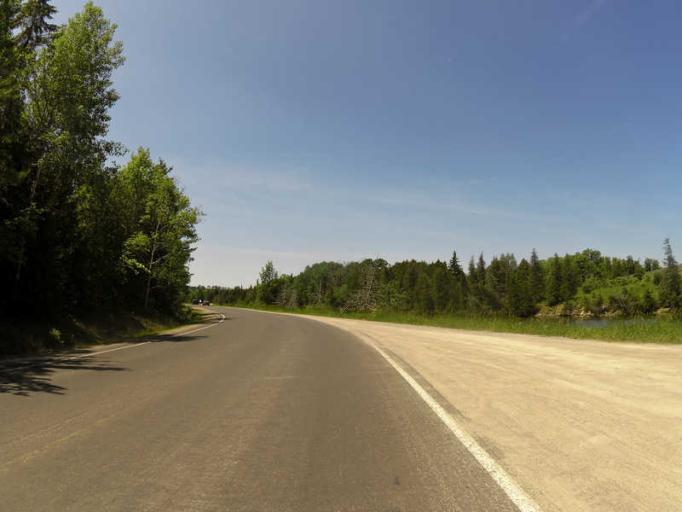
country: CA
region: Ontario
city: Peterborough
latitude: 44.3814
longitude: -78.2761
